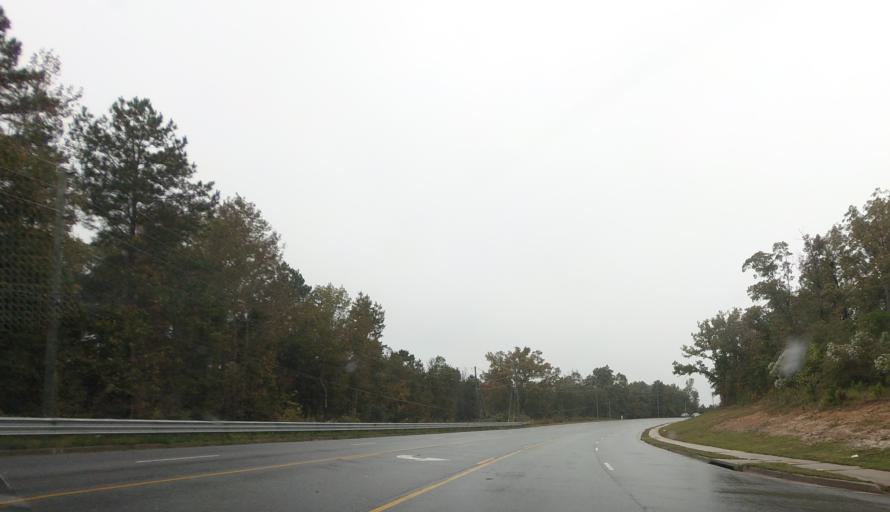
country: US
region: Georgia
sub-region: Houston County
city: Centerville
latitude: 32.6109
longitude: -83.6679
